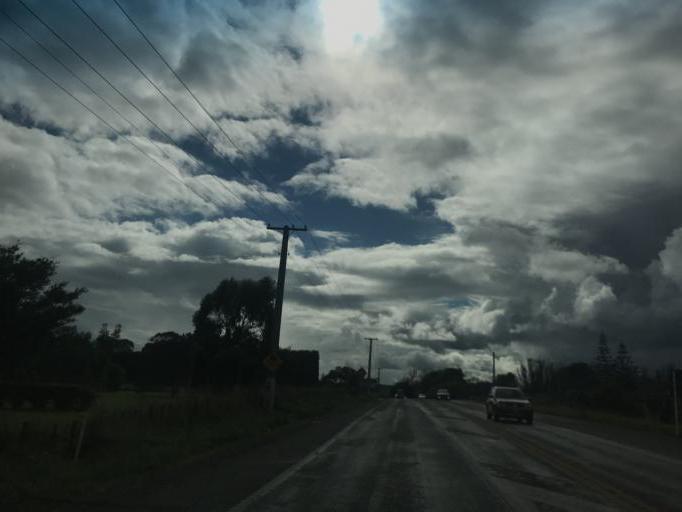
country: NZ
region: Wellington
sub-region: Kapiti Coast District
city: Otaki
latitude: -40.7751
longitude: 175.1428
